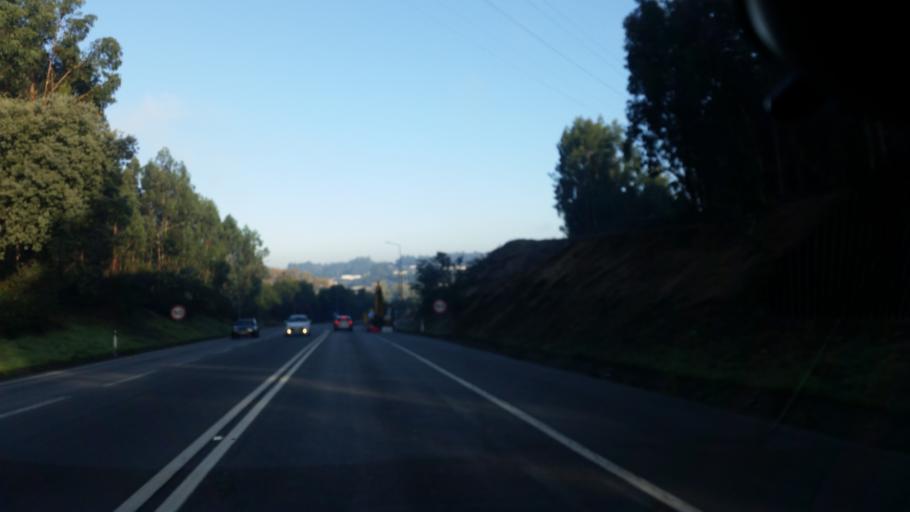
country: PT
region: Porto
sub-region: Santo Tirso
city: Sao Miguel do Couto
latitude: 41.3400
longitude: -8.4672
